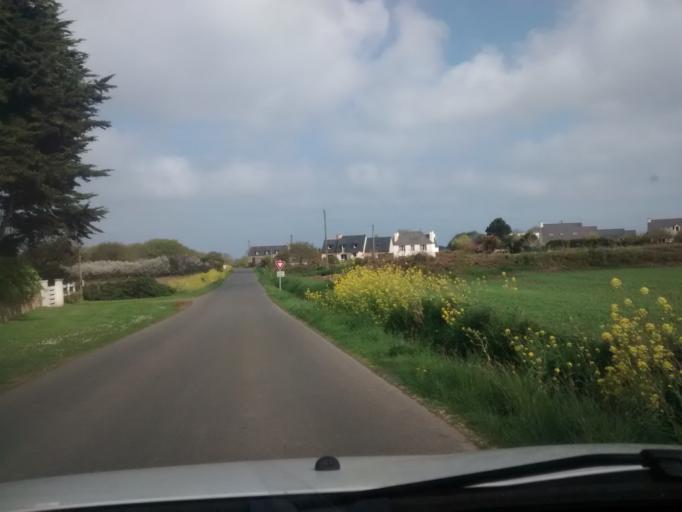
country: FR
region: Brittany
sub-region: Departement des Cotes-d'Armor
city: Penvenan
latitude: 48.8270
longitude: -3.3073
